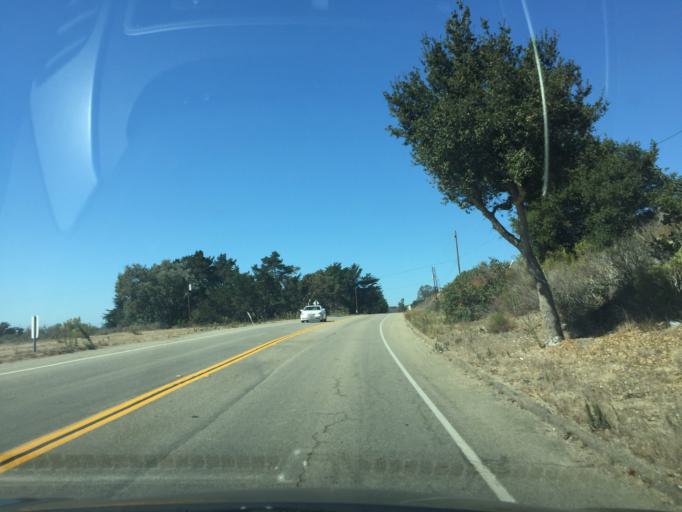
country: US
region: California
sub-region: Santa Barbara County
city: Mission Hills
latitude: 34.6727
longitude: -120.4337
